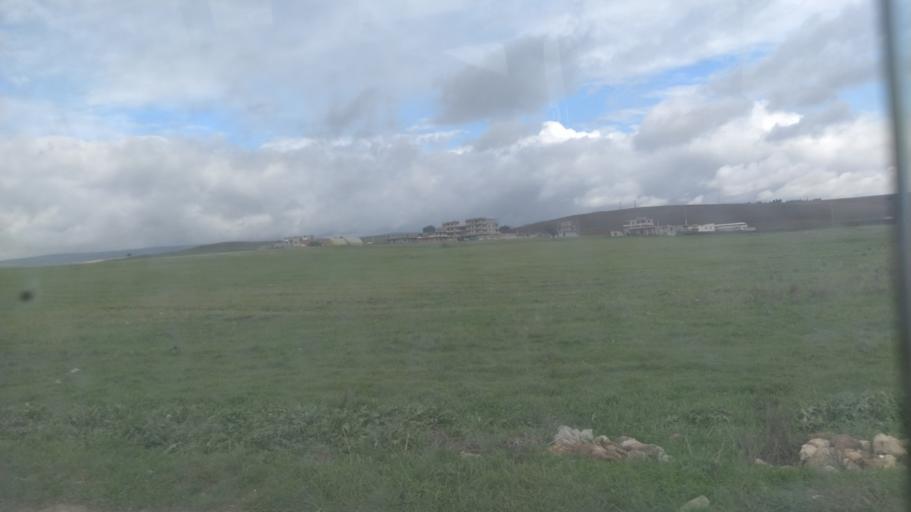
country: DZ
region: Constantine
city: El Khroub
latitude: 36.3012
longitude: 6.6977
